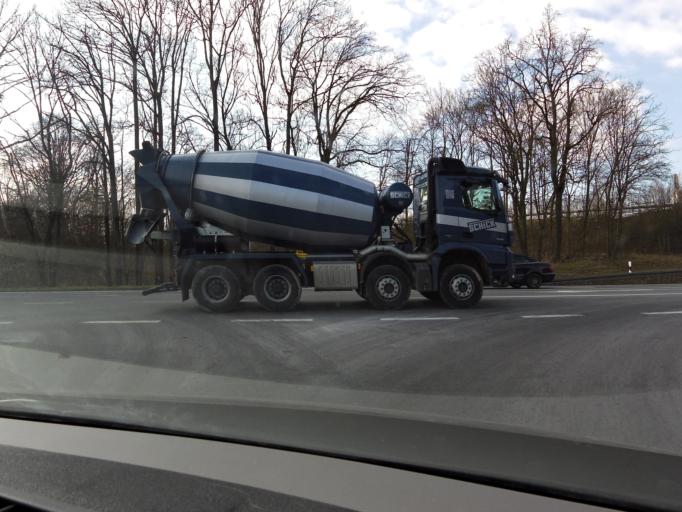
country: DE
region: Bavaria
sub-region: Regierungsbezirk Unterfranken
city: Werneck
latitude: 50.0012
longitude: 10.1185
